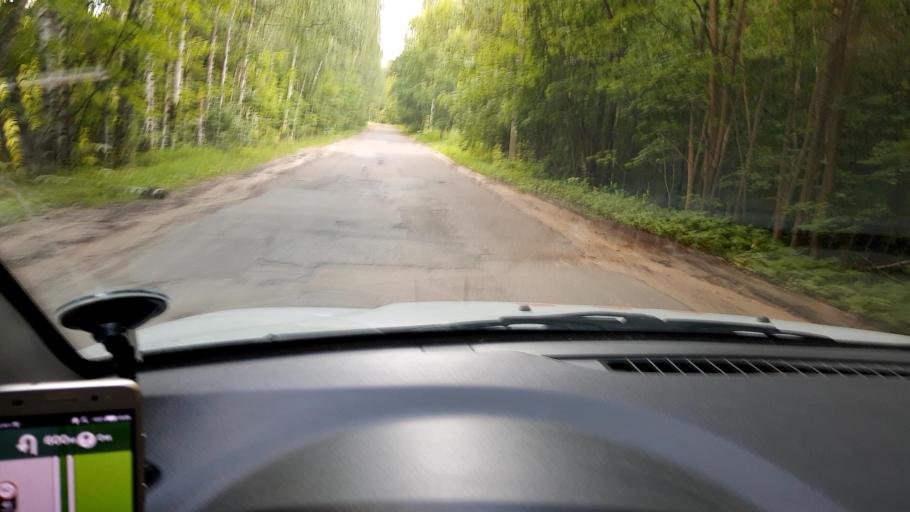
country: RU
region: Nizjnij Novgorod
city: Afonino
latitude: 56.2031
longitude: 44.0242
